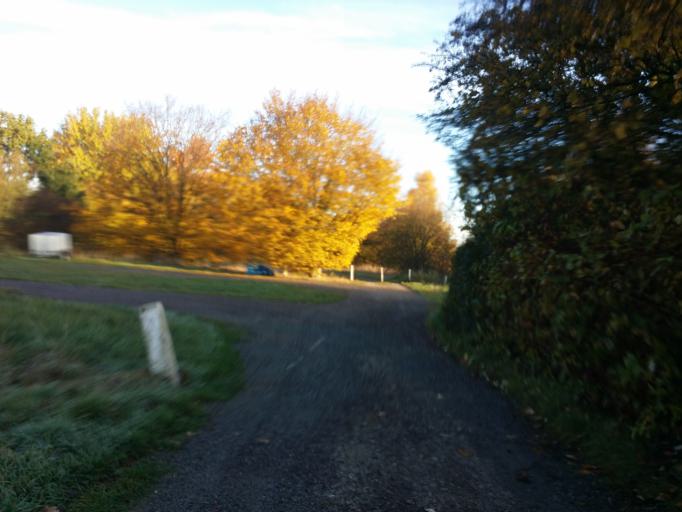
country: DE
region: Bremen
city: Bremen
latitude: 53.0397
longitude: 8.8086
